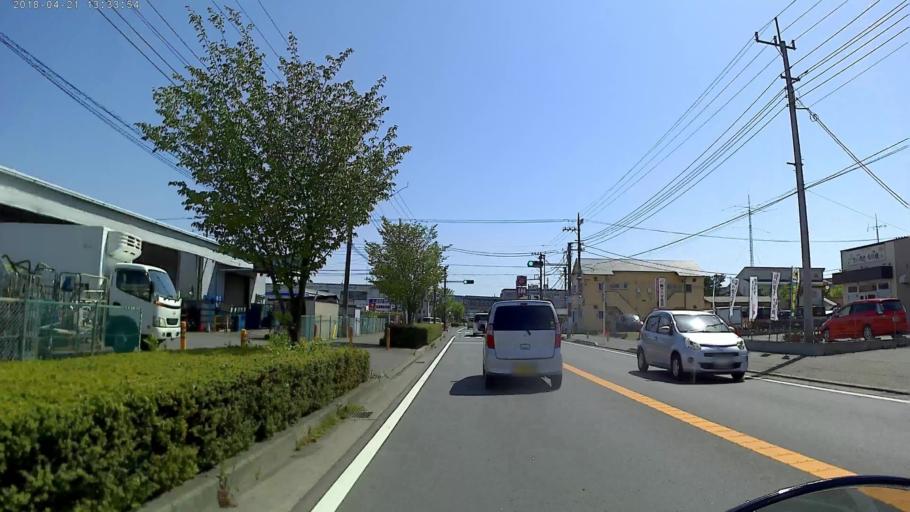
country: JP
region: Kanagawa
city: Atsugi
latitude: 35.3958
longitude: 139.3807
